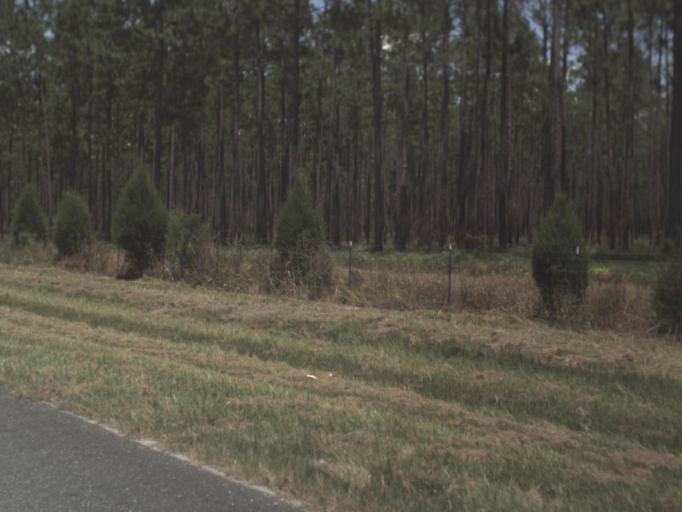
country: US
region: Florida
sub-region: Columbia County
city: Lake City
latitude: 30.1084
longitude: -82.7384
